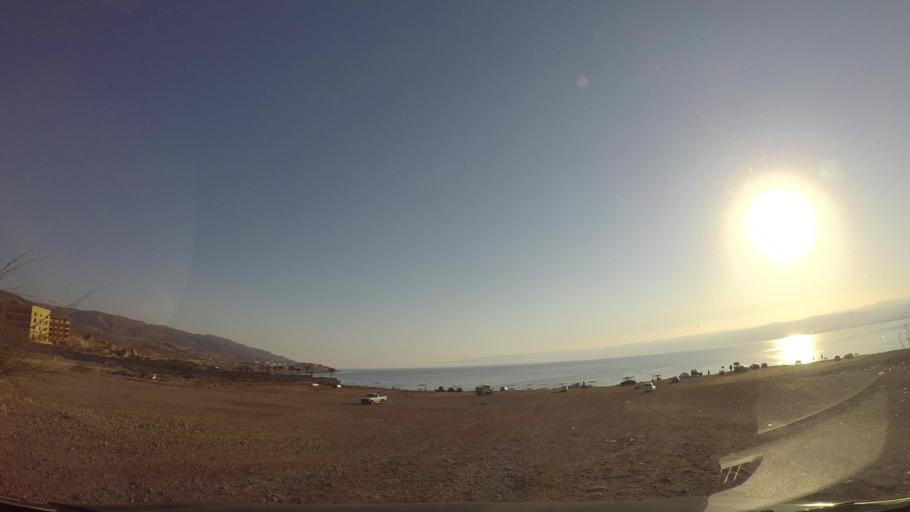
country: PS
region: West Bank
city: Jericho
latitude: 31.7483
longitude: 35.5918
